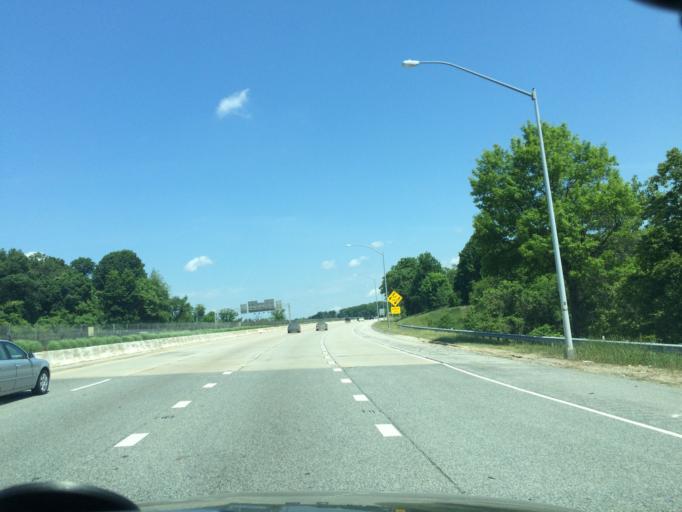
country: US
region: Maryland
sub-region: Baltimore County
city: Pikesville
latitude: 39.3768
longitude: -76.7521
